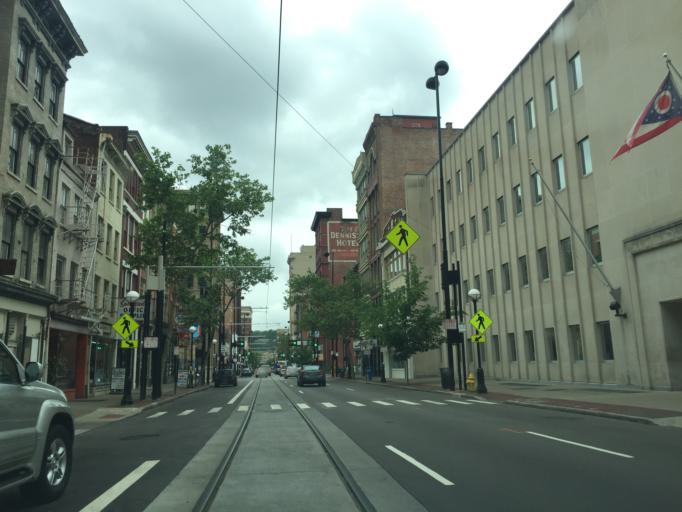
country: US
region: Kentucky
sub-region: Campbell County
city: Newport
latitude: 39.1034
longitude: -84.5102
